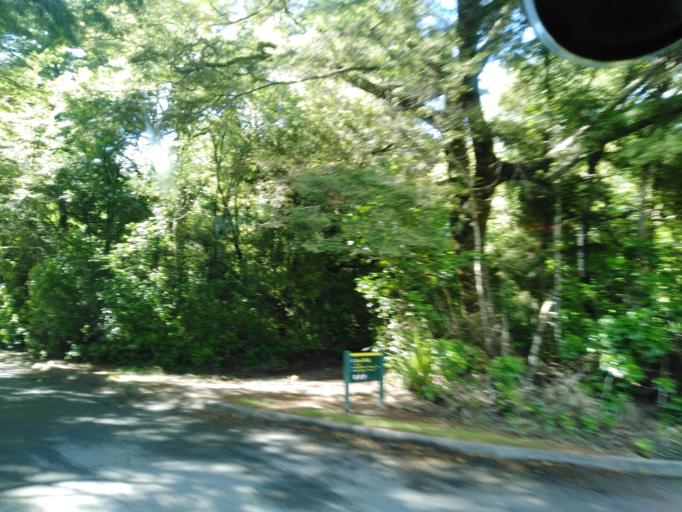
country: NZ
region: Nelson
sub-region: Nelson City
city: Nelson
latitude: -41.2991
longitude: 173.5721
